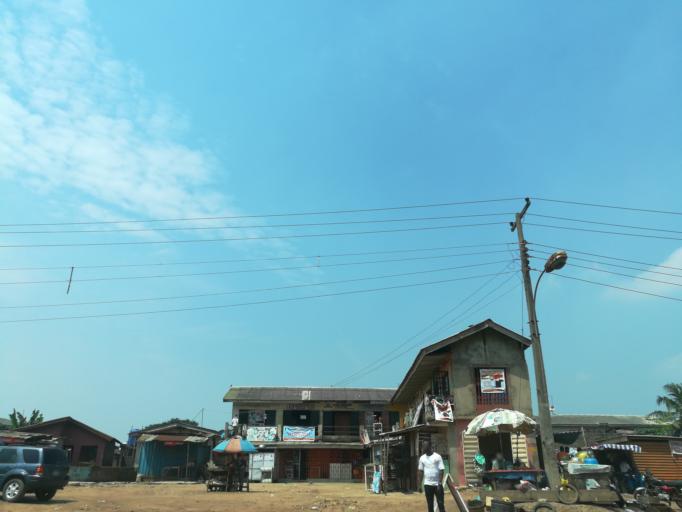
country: NG
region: Lagos
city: Ikorodu
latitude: 6.6474
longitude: 3.4783
